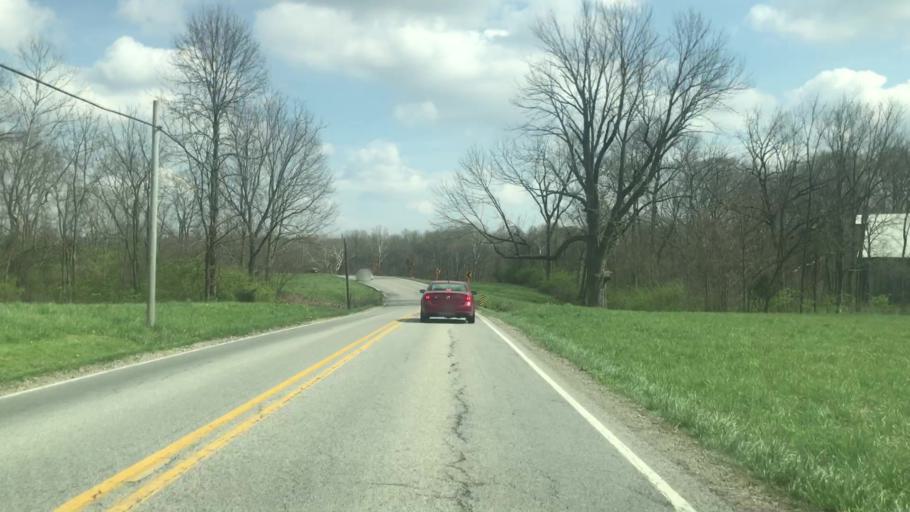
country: US
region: Indiana
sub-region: Johnson County
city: Waterloo
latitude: 39.5537
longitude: -86.2171
